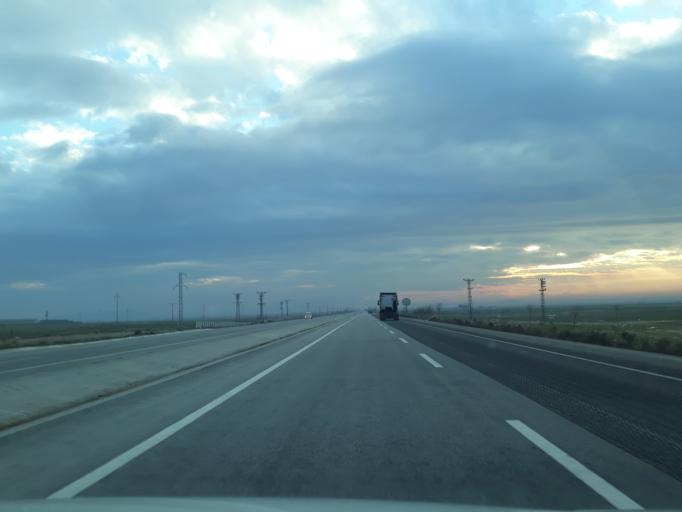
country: TR
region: Konya
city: Hotamis
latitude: 37.7107
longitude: 33.2802
